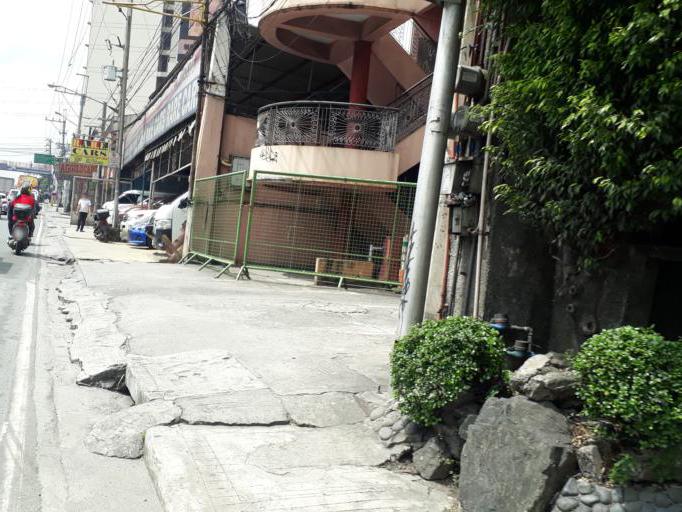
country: PH
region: Calabarzon
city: Bagong Pagasa
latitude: 14.6788
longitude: 121.0319
